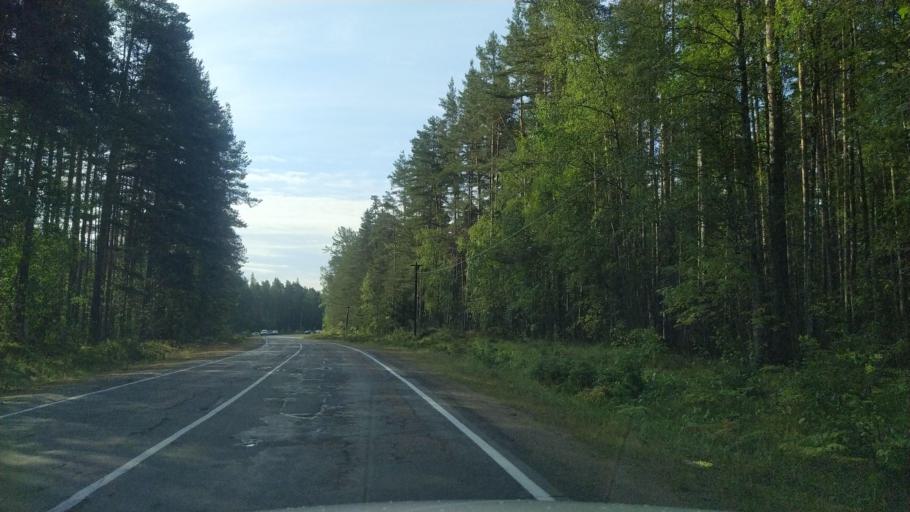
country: RU
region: Leningrad
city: Priozersk
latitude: 60.9965
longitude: 30.2509
